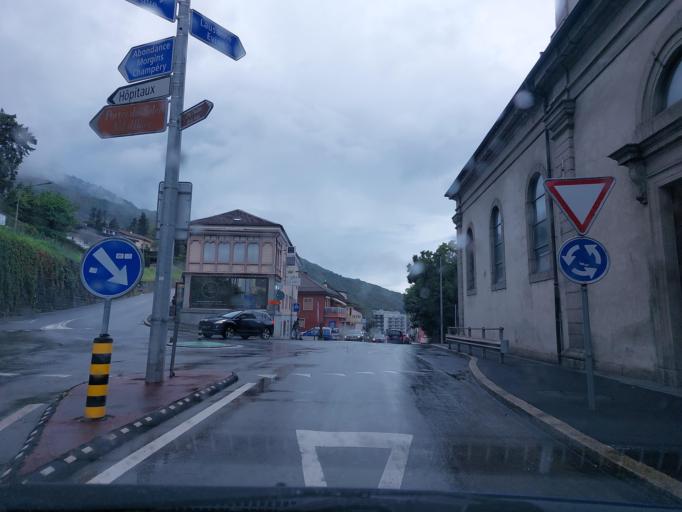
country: CH
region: Valais
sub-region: Monthey District
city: Monthey
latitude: 46.2526
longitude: 6.9468
